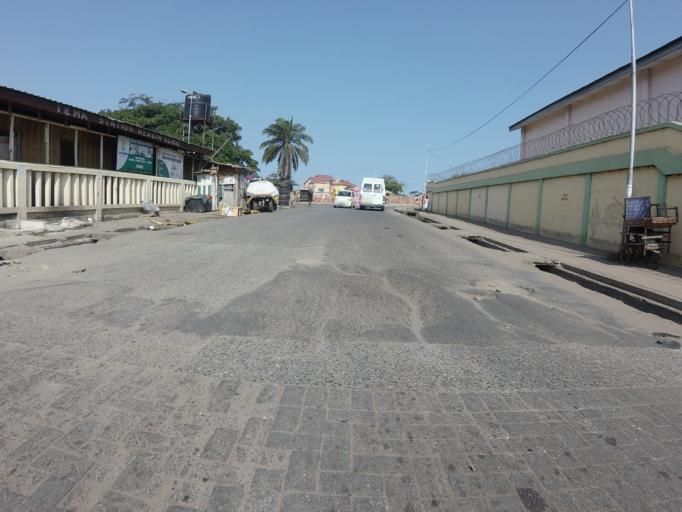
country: GH
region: Greater Accra
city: Accra
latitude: 5.5482
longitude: -0.2009
